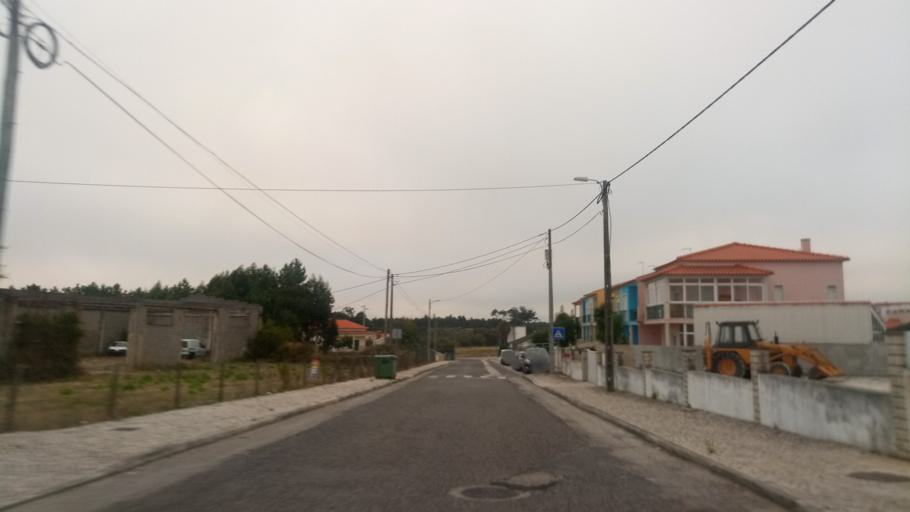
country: PT
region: Leiria
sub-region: Caldas da Rainha
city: Caldas da Rainha
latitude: 39.4299
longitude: -9.1542
